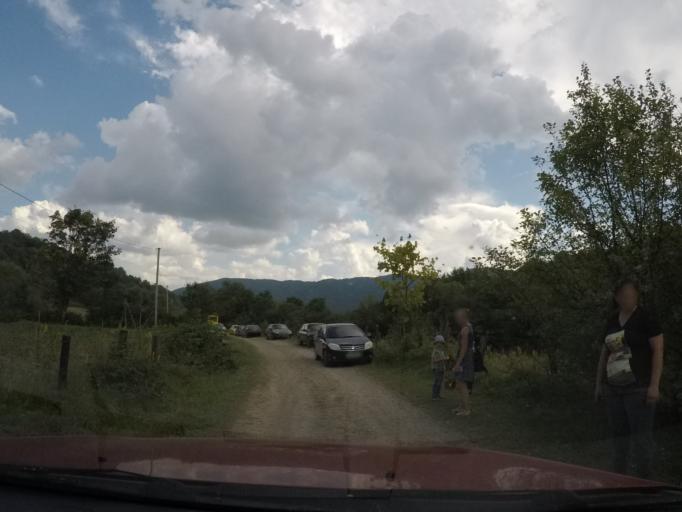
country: UA
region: Zakarpattia
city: Velykyi Bereznyi
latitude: 49.0411
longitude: 22.5813
